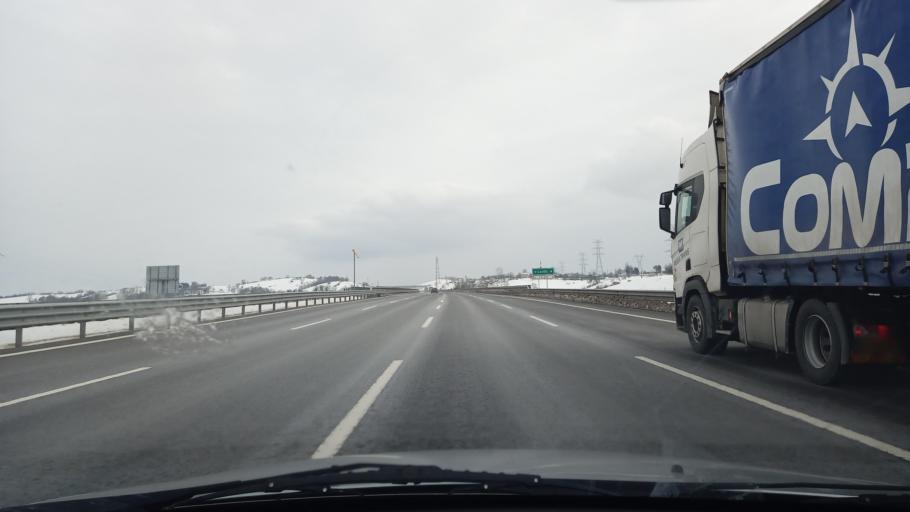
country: TR
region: Kocaeli
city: Korfez
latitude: 40.8658
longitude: 29.7986
